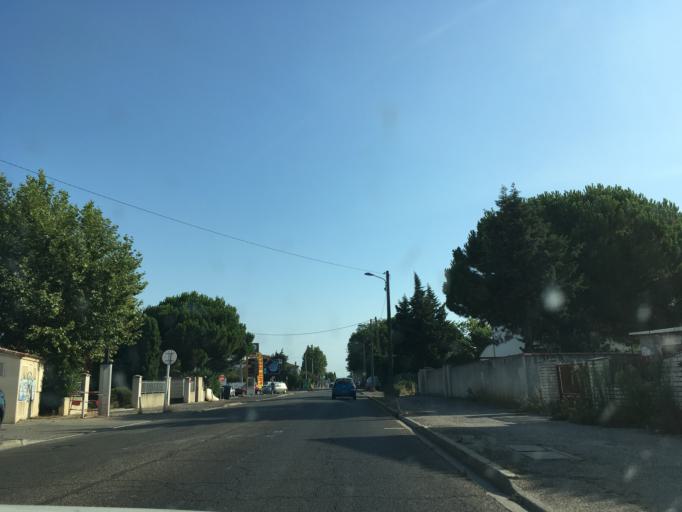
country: FR
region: Provence-Alpes-Cote d'Azur
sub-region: Departement des Bouches-du-Rhone
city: Arles
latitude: 43.6900
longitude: 4.6371
